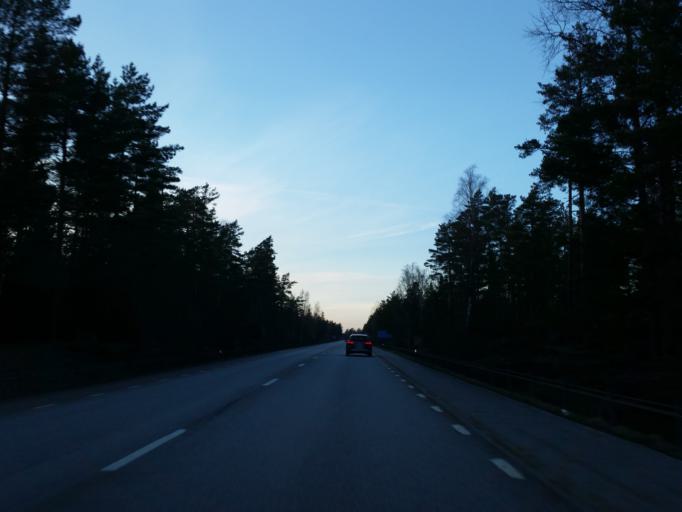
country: SE
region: Kalmar
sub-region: Vasterviks Kommun
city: Ankarsrum
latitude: 57.5197
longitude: 16.4967
